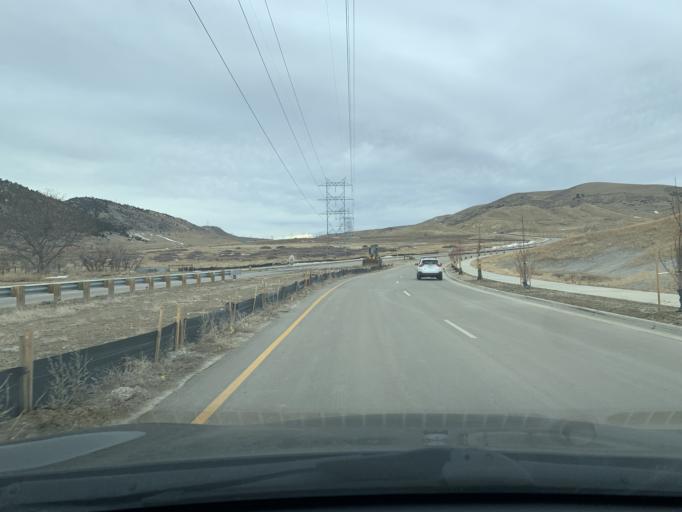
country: US
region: Colorado
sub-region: Jefferson County
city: West Pleasant View
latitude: 39.6780
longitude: -105.1837
